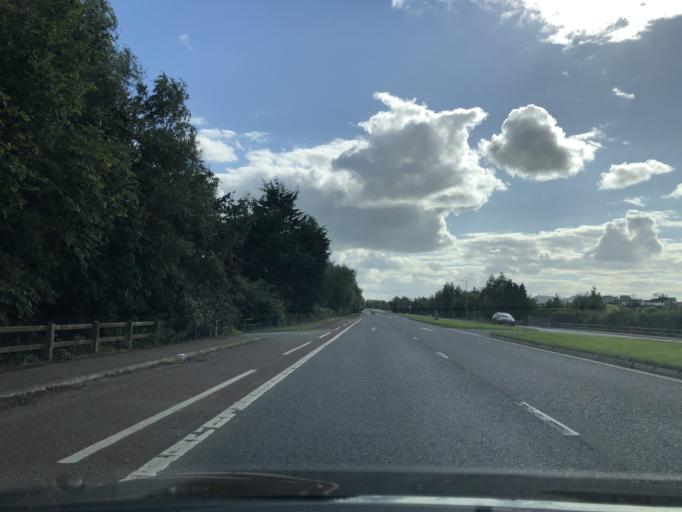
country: GB
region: Northern Ireland
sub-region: Ards District
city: Comber
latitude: 54.5569
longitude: -5.7179
